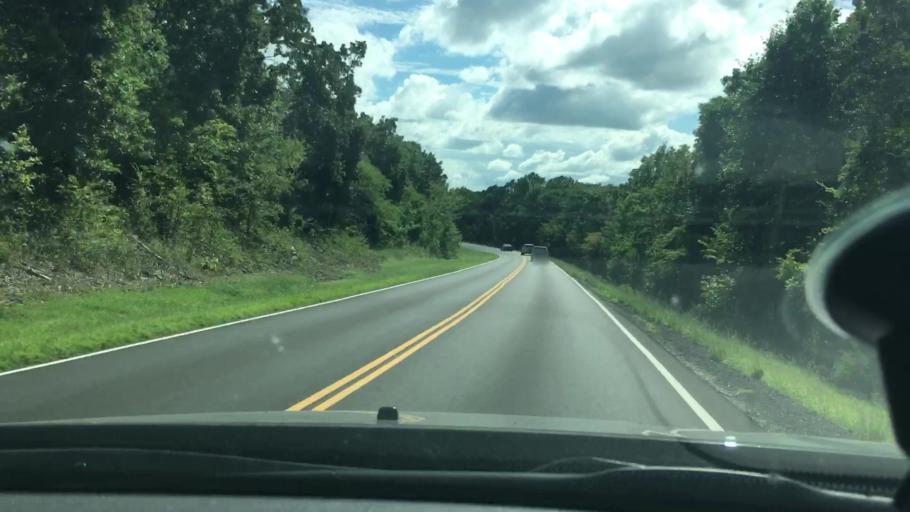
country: US
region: Oklahoma
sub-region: Sequoyah County
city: Vian
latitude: 35.6597
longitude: -94.9507
